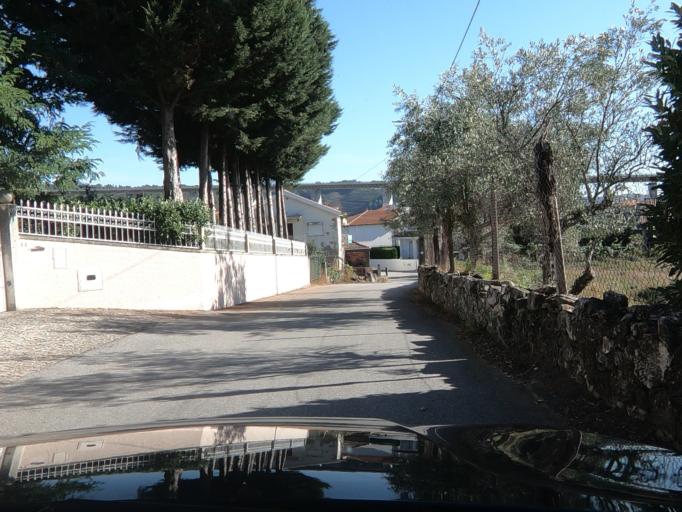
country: PT
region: Vila Real
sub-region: Vila Real
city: Vila Real
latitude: 41.2821
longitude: -7.7439
